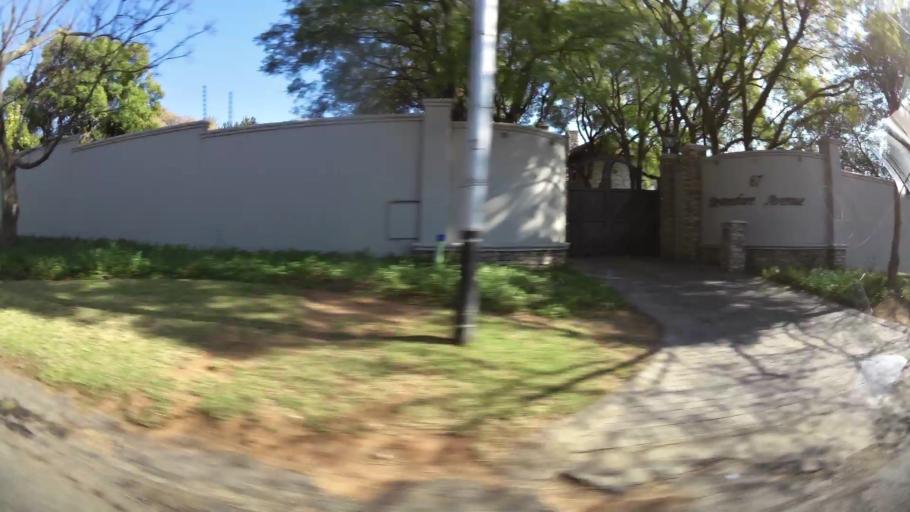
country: ZA
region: Gauteng
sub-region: City of Johannesburg Metropolitan Municipality
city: Midrand
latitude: -26.0531
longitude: 28.0477
